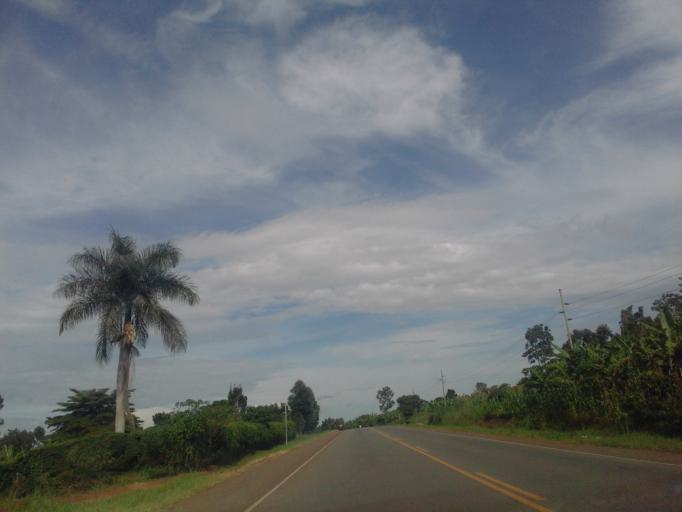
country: UG
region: Central Region
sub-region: Lwengo District
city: Lwengo
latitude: -0.3672
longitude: 31.5365
